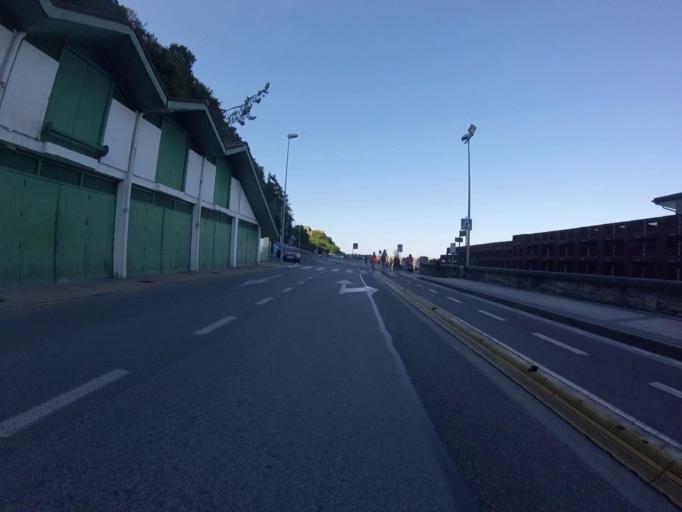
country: ES
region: Basque Country
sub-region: Provincia de Guipuzcoa
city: Fuenterrabia
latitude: 43.3877
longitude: -1.7914
